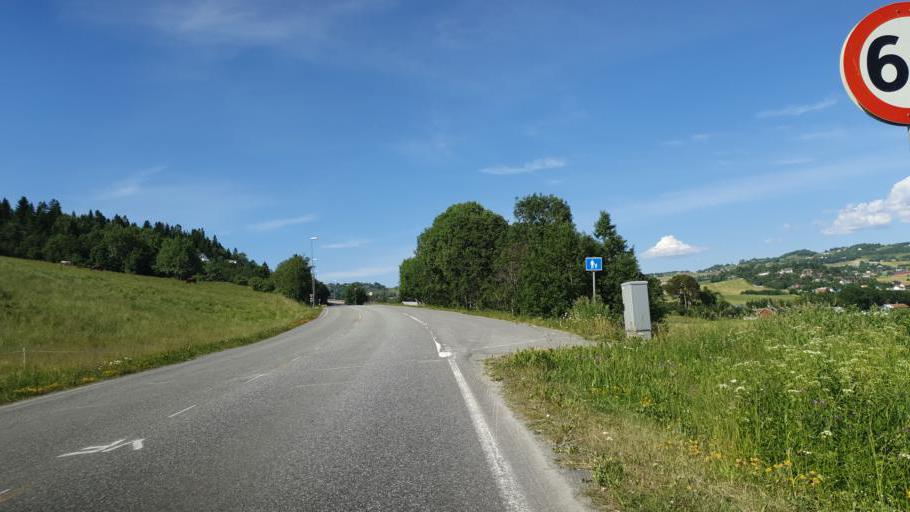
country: NO
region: Nord-Trondelag
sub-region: Leksvik
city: Leksvik
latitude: 63.6631
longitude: 10.6080
